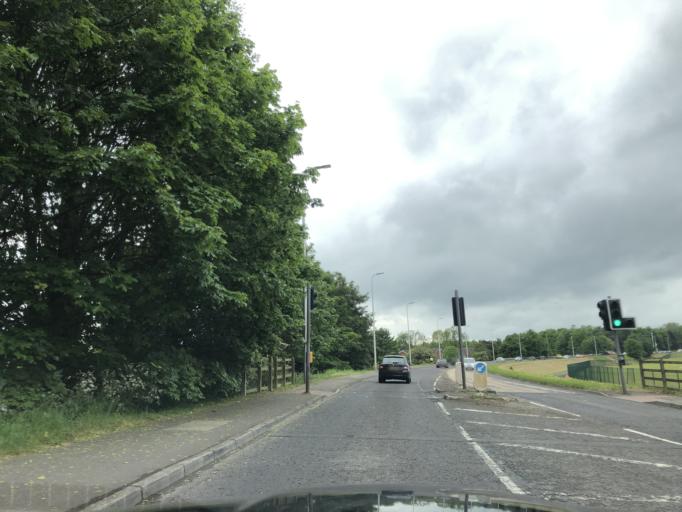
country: GB
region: Northern Ireland
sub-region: Lisburn District
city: Lisburn
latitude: 54.5168
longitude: -6.0675
